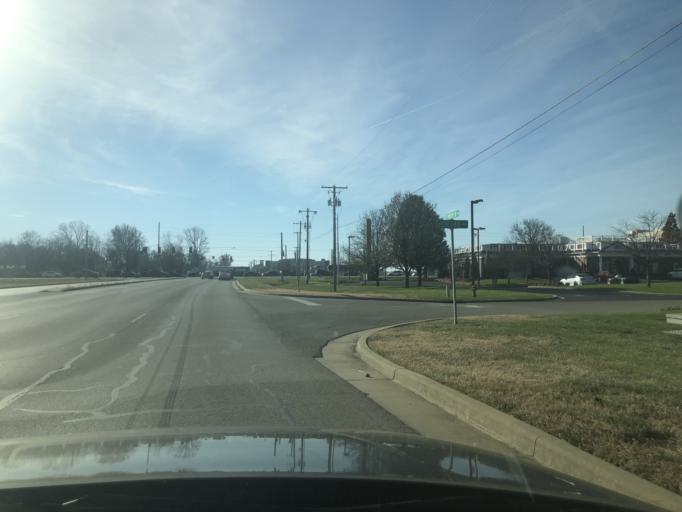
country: US
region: Indiana
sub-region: Warrick County
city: Newburgh
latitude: 37.9782
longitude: -87.4413
